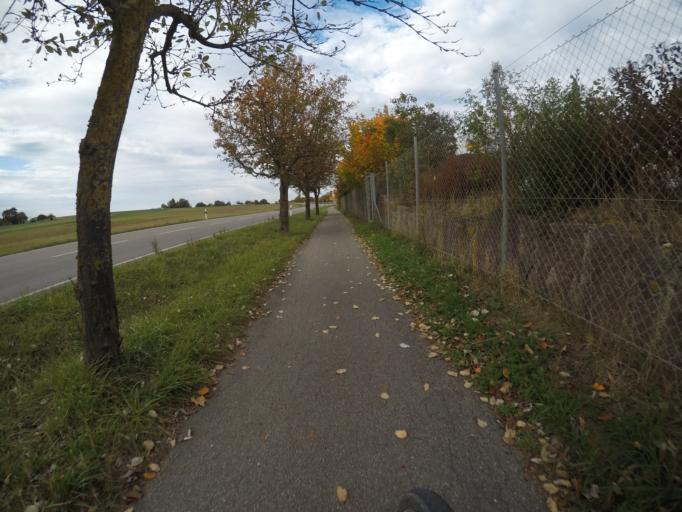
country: DE
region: Baden-Wuerttemberg
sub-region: Regierungsbezirk Stuttgart
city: Nufringen
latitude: 48.6297
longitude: 8.8935
